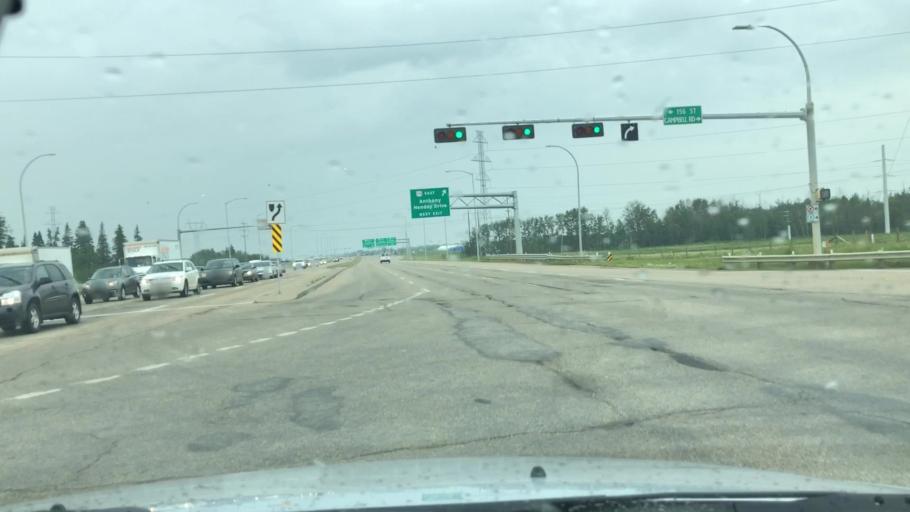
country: CA
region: Alberta
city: St. Albert
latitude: 53.6117
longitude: -113.5913
